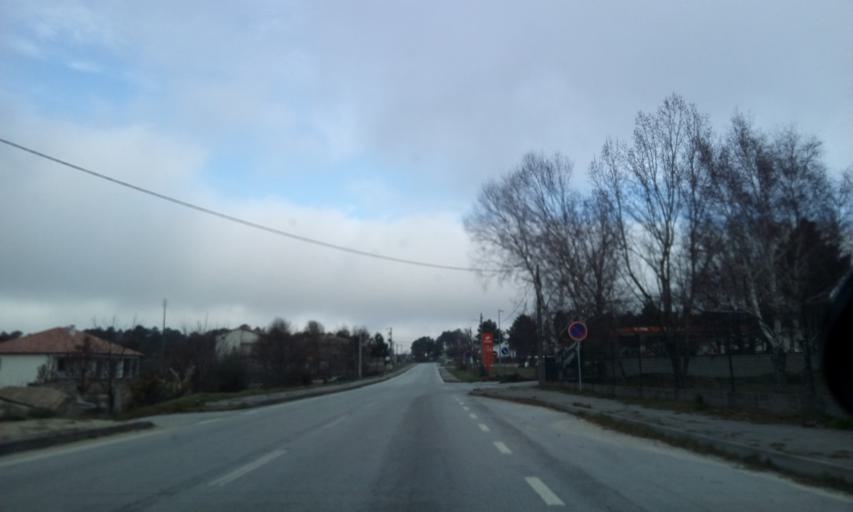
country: PT
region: Guarda
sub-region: Aguiar da Beira
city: Aguiar da Beira
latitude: 40.7411
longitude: -7.4961
